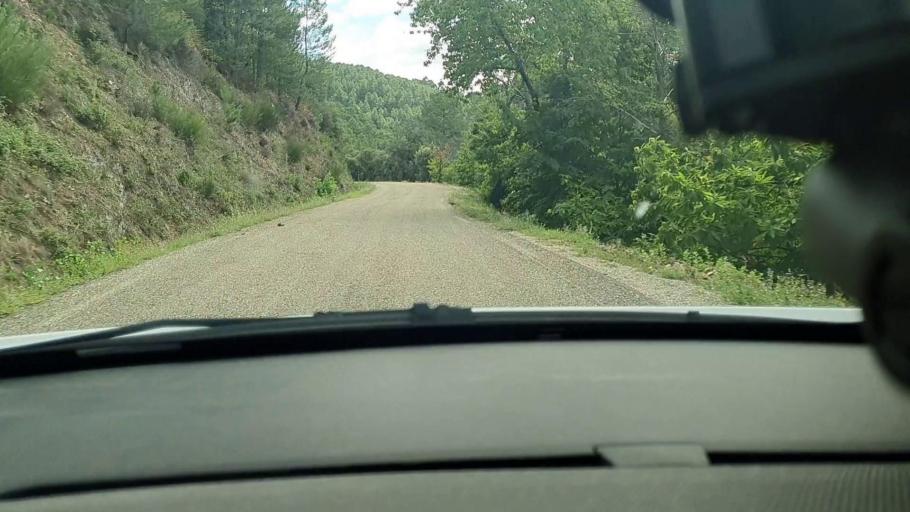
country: FR
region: Languedoc-Roussillon
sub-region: Departement du Gard
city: Branoux-les-Taillades
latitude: 44.2791
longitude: 3.9757
